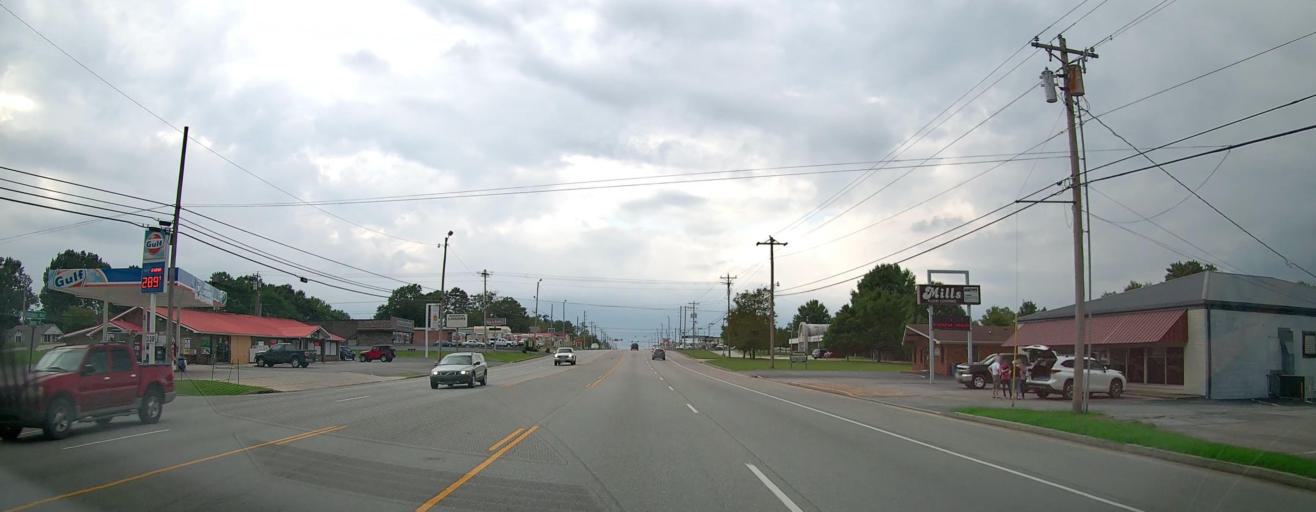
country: US
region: Tennessee
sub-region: Coffee County
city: Manchester
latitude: 35.4662
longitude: -86.0695
